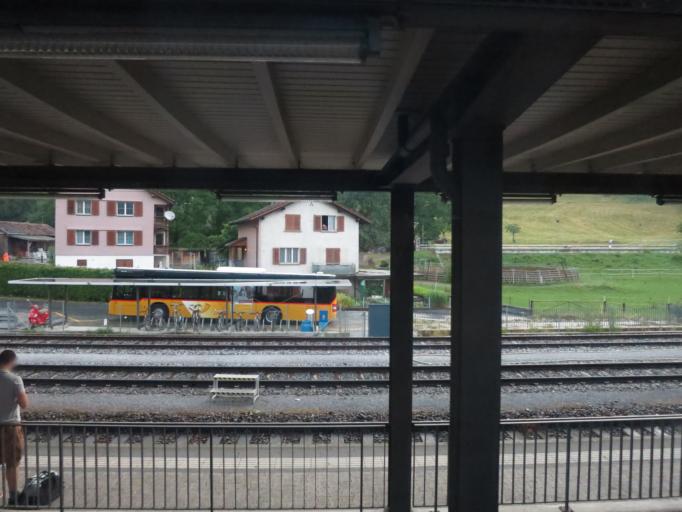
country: CH
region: Glarus
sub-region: Glarus
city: Niederurnen
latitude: 47.1369
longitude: 9.0597
